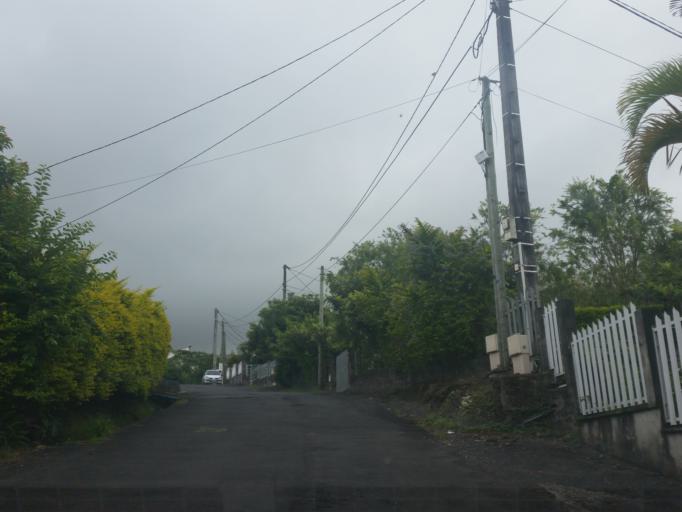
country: RE
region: Reunion
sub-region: Reunion
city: Le Tampon
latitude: -21.2354
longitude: 55.5207
